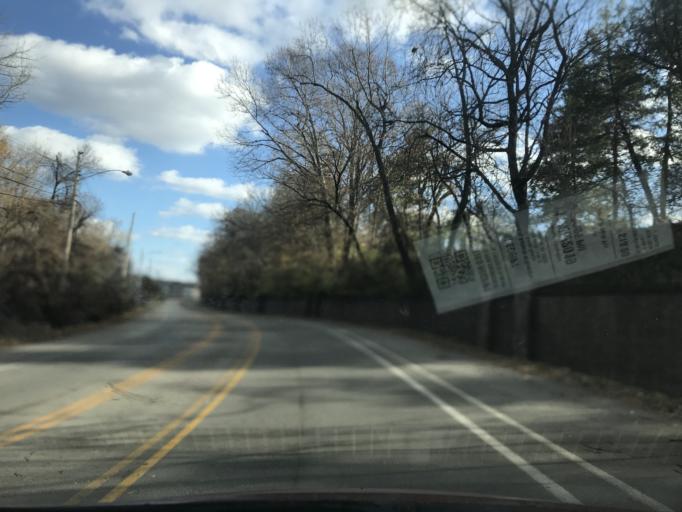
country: US
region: Indiana
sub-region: Clark County
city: Jeffersonville
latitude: 38.2482
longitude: -85.7111
